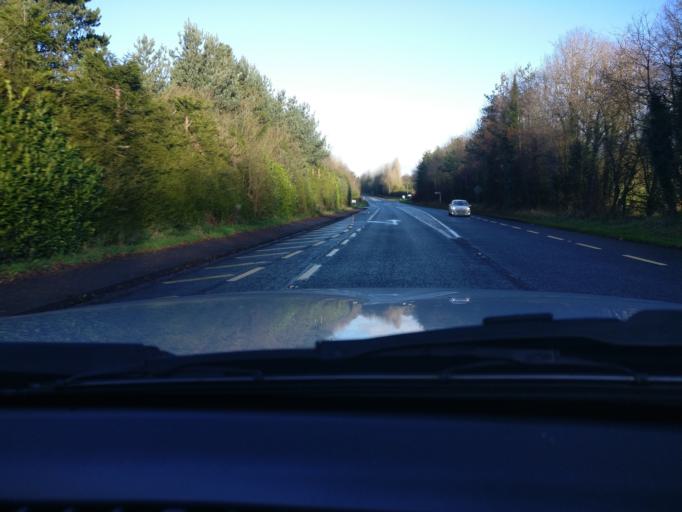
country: IE
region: Leinster
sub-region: An Iarmhi
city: An Muileann gCearr
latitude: 53.5367
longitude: -7.3079
